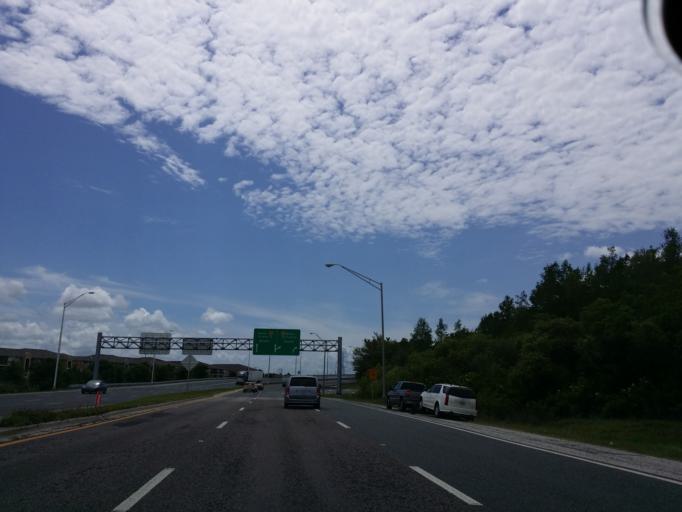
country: US
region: Florida
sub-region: Orange County
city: Tangelo Park
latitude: 28.4772
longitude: -81.4456
